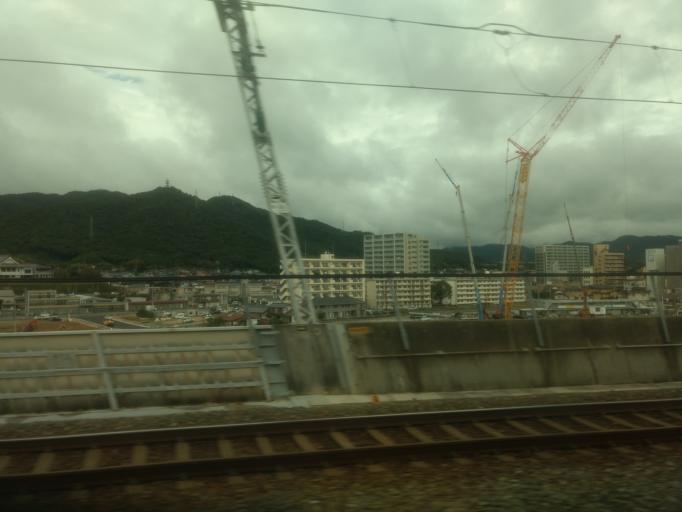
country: JP
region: Yamaguchi
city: Ogori-shimogo
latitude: 34.0912
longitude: 131.3938
